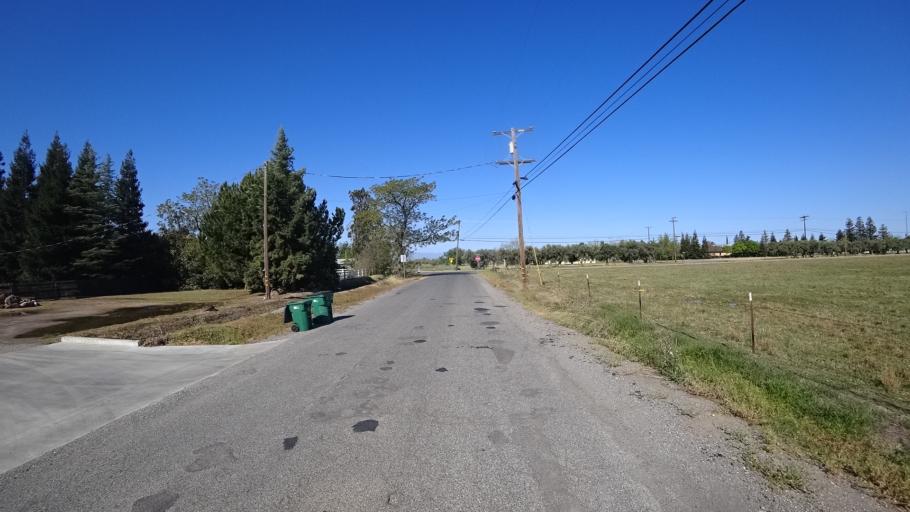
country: US
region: California
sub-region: Glenn County
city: Orland
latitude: 39.7290
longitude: -122.1681
